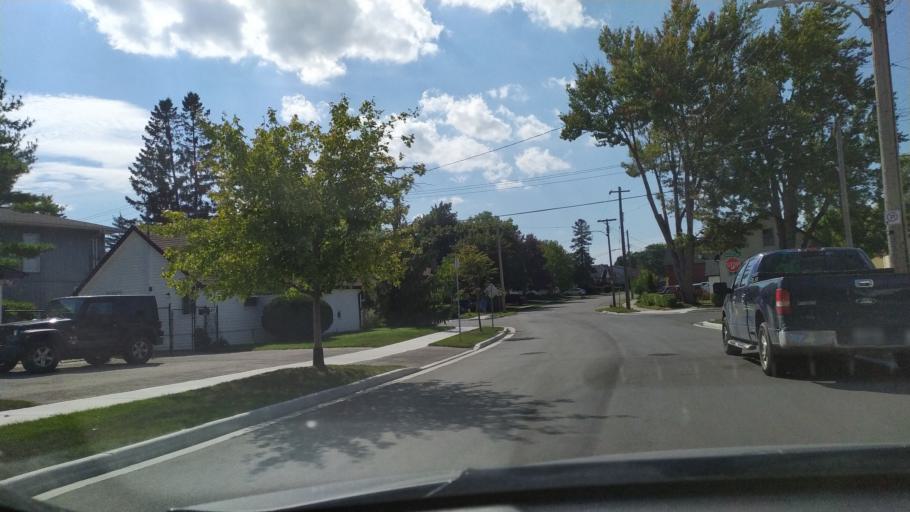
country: CA
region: Ontario
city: London
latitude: 42.9660
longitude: -81.2639
